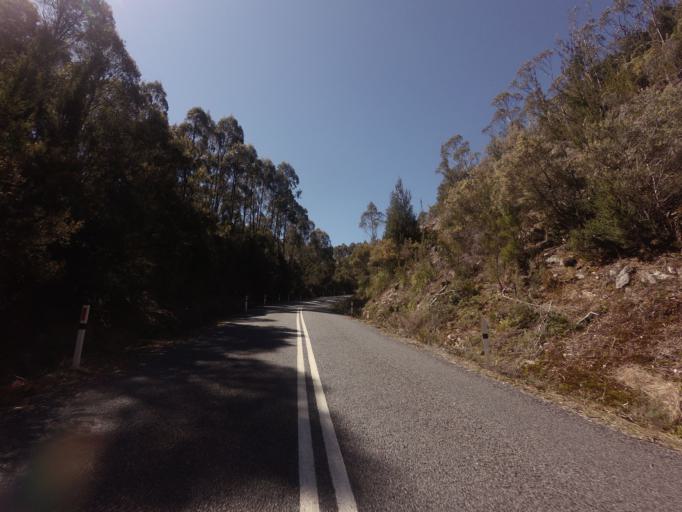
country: AU
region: Tasmania
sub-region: Huon Valley
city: Geeveston
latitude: -42.8144
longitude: 146.3771
